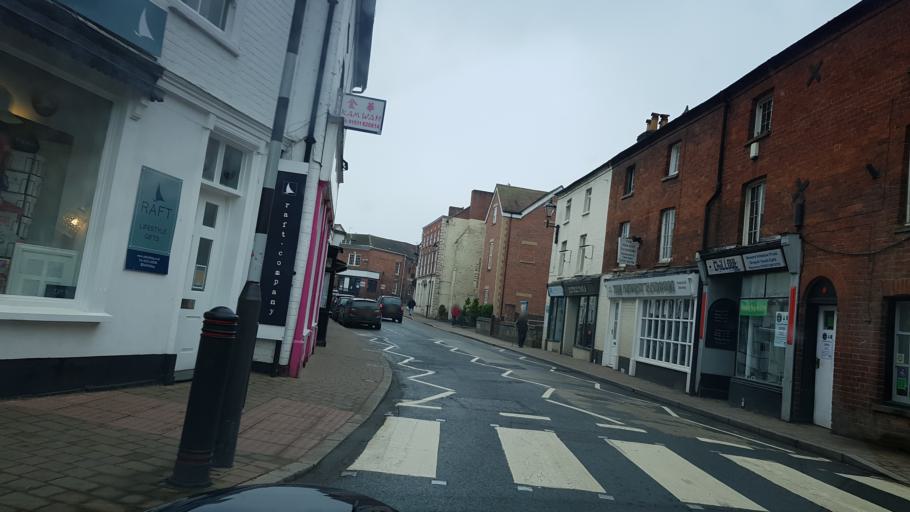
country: GB
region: England
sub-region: Gloucestershire
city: Newent
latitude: 51.9313
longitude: -2.4065
